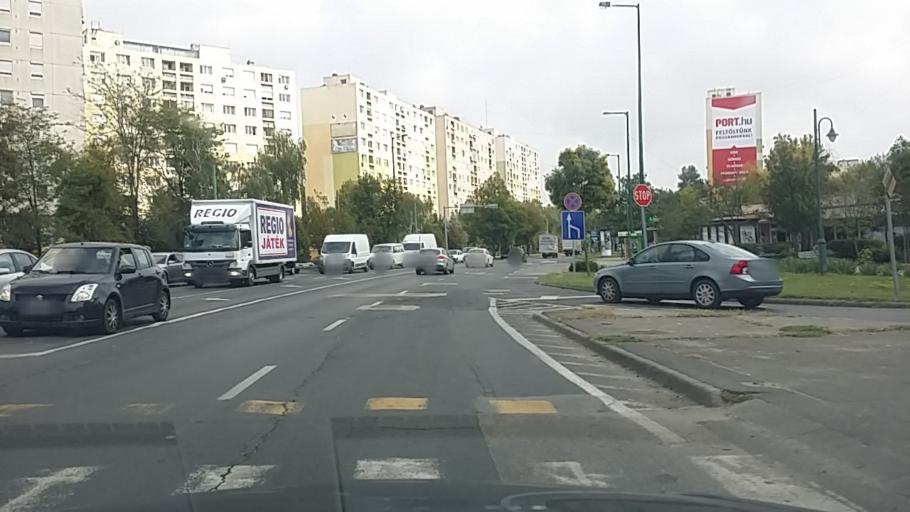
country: HU
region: Csongrad
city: Szeged
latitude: 46.2727
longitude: 20.1594
